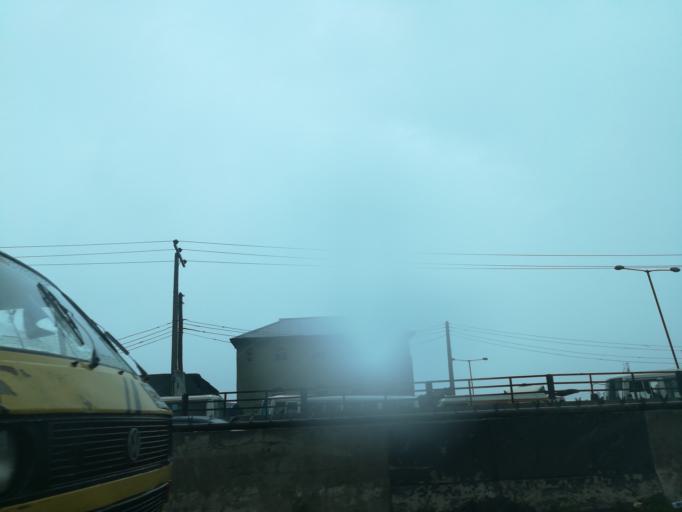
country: NG
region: Lagos
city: Ojota
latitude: 6.6082
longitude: 3.3959
